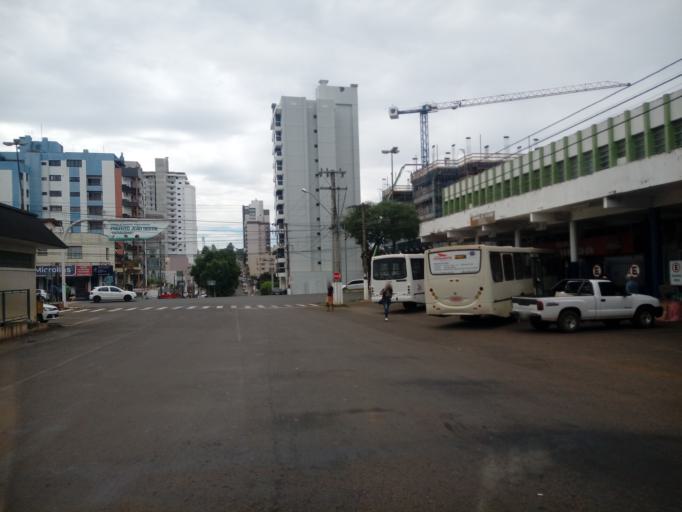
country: BR
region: Santa Catarina
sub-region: Chapeco
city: Chapeco
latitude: -27.1062
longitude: -52.6124
